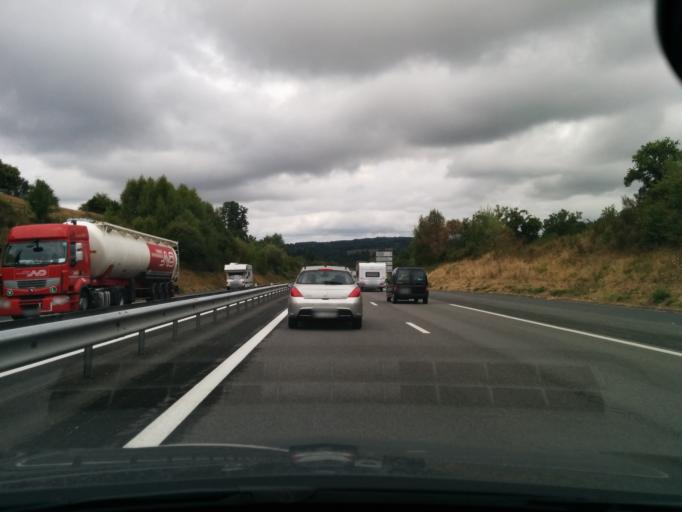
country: FR
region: Limousin
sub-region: Departement de la Correze
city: Vigeois
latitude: 45.3271
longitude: 1.5721
